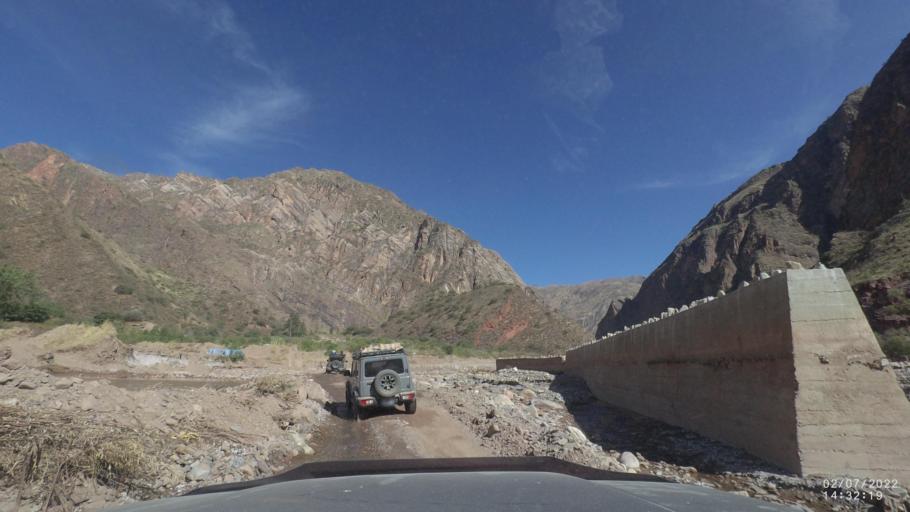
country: BO
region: Cochabamba
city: Irpa Irpa
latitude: -17.8361
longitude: -66.4148
